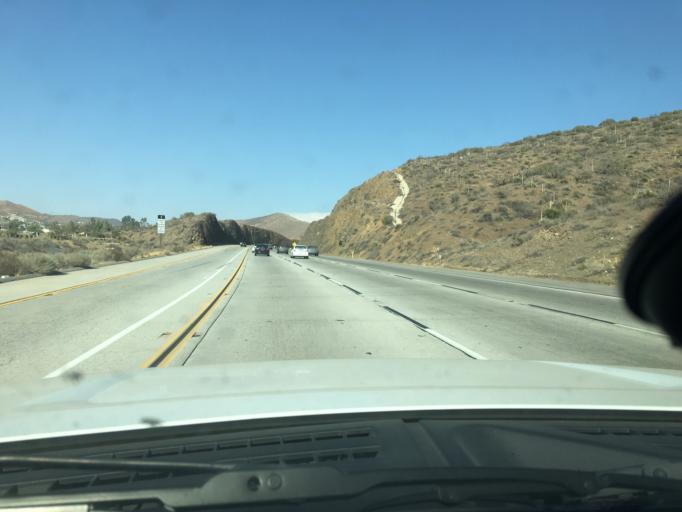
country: US
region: California
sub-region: Los Angeles County
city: Acton
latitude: 34.4923
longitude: -118.1781
